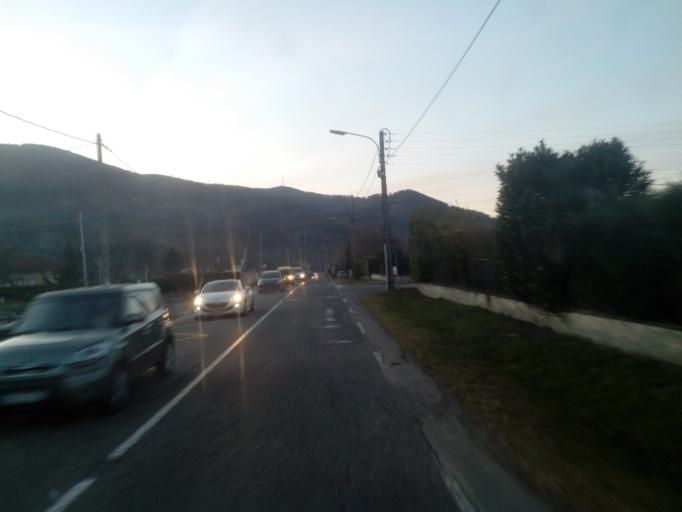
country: FR
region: Midi-Pyrenees
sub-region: Departement de l'Ariege
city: Saint-Paul-de-Jarrat
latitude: 42.9171
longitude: 1.6455
